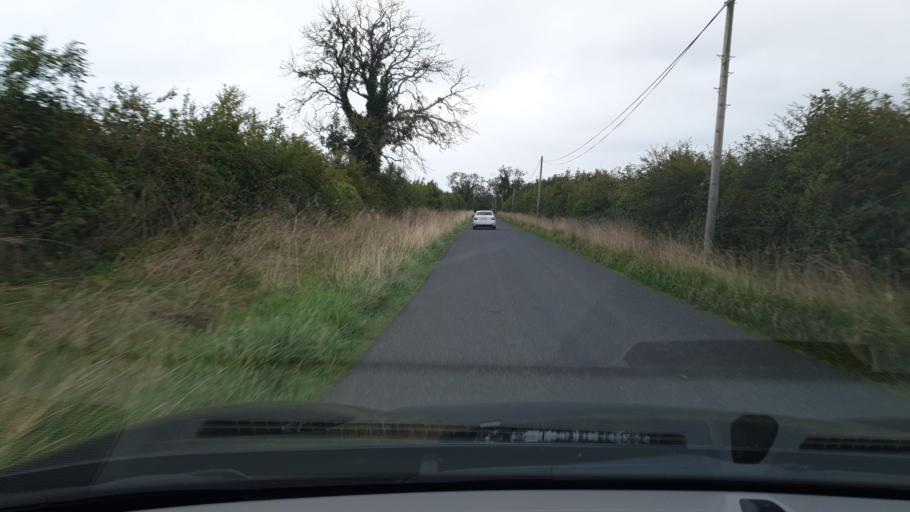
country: IE
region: Leinster
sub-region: An Mhi
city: Dunshaughlin
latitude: 53.5444
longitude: -6.5379
